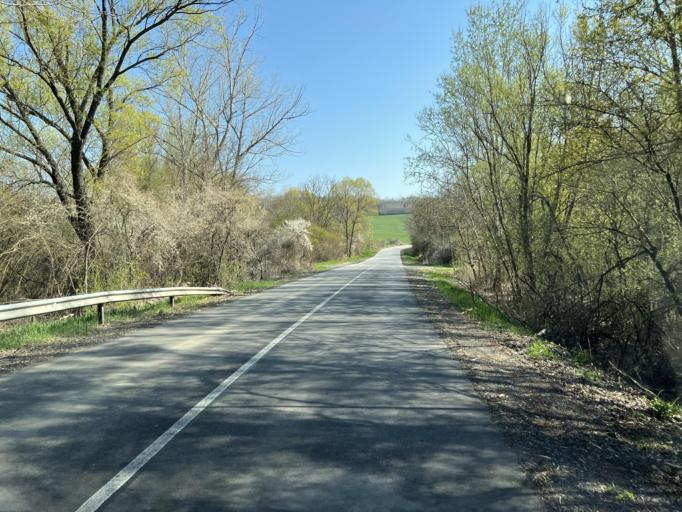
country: HU
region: Pest
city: Orbottyan
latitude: 47.7313
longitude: 19.2693
